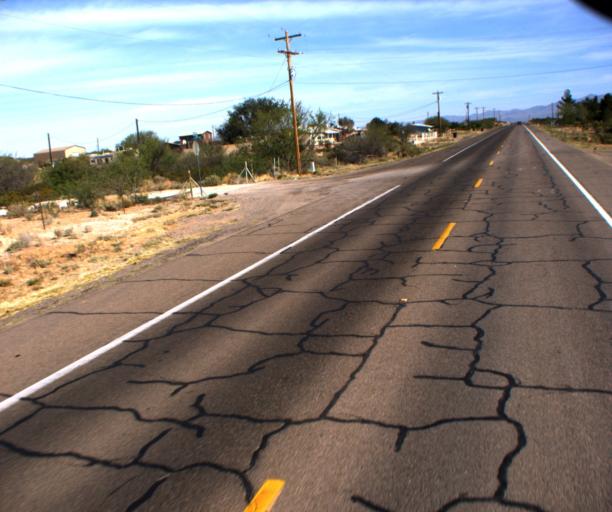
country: US
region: Arizona
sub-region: Graham County
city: Swift Trail Junction
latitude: 32.7052
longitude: -109.7078
